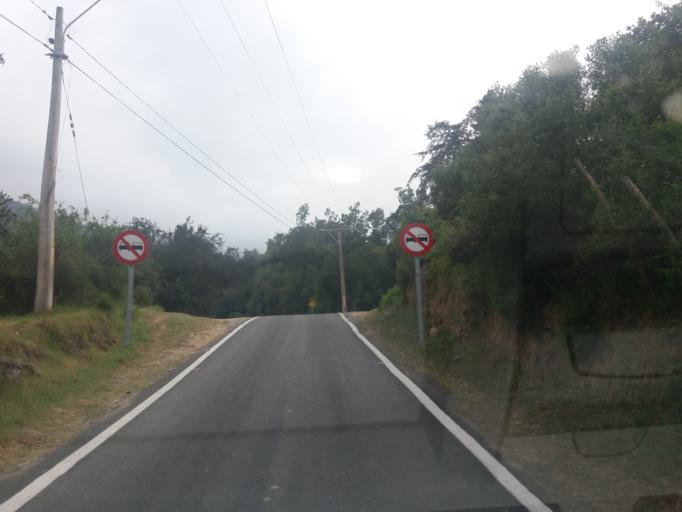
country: CL
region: Valparaiso
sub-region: Provincia de Marga Marga
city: Limache
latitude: -33.0255
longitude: -71.0748
